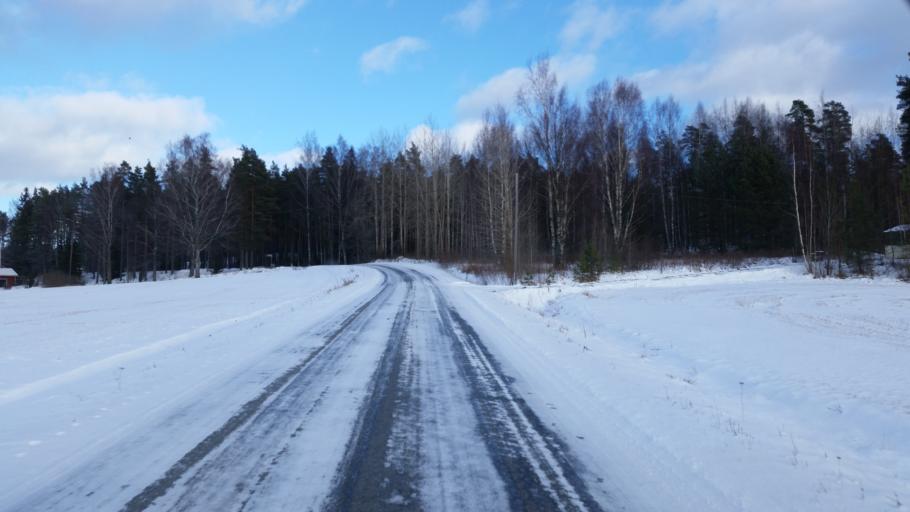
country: FI
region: Varsinais-Suomi
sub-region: Salo
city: Muurla
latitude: 60.3305
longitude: 23.2861
